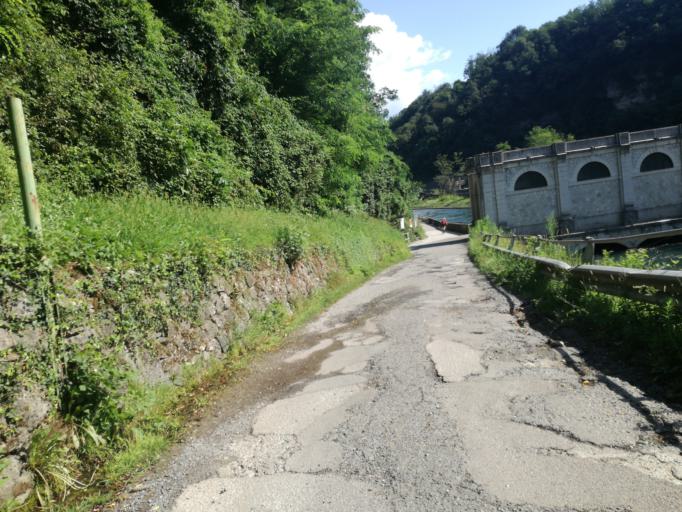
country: IT
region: Lombardy
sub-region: Provincia di Lecco
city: Paderno d'Adda
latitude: 45.6861
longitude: 9.4502
